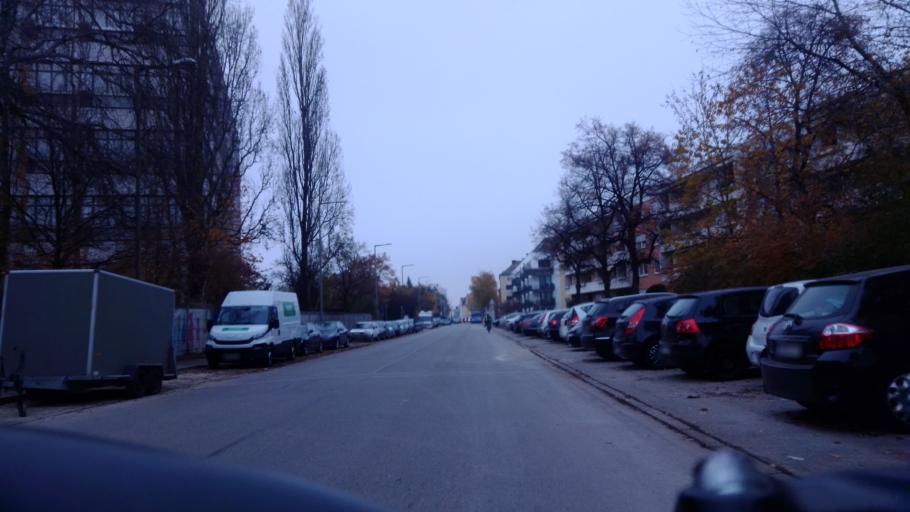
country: DE
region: Bavaria
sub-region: Upper Bavaria
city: Pullach im Isartal
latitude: 48.0965
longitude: 11.5378
